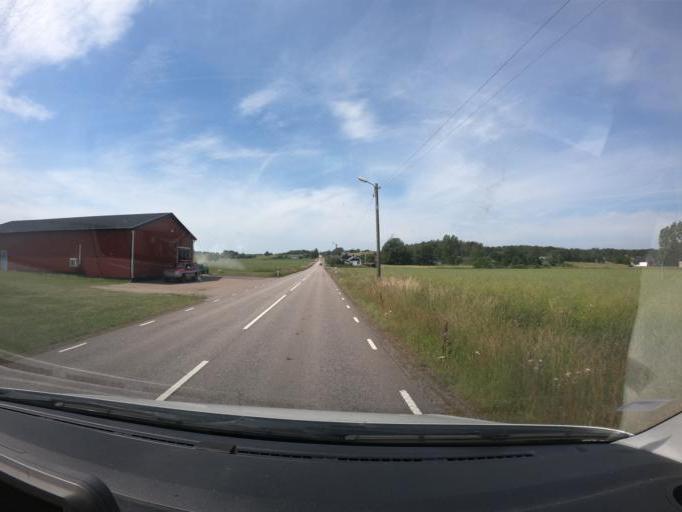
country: SE
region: Skane
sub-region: Bastads Kommun
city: Bastad
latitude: 56.4364
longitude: 12.7888
